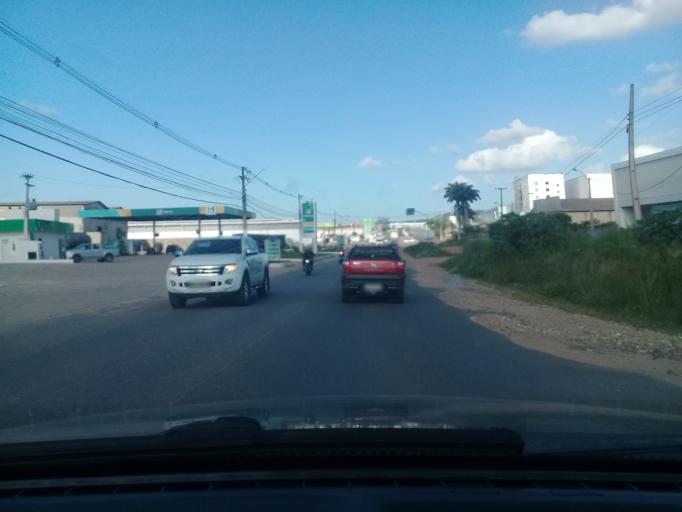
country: BR
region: Pernambuco
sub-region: Vitoria De Santo Antao
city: Vitoria de Santo Antao
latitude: -8.1150
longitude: -35.2743
